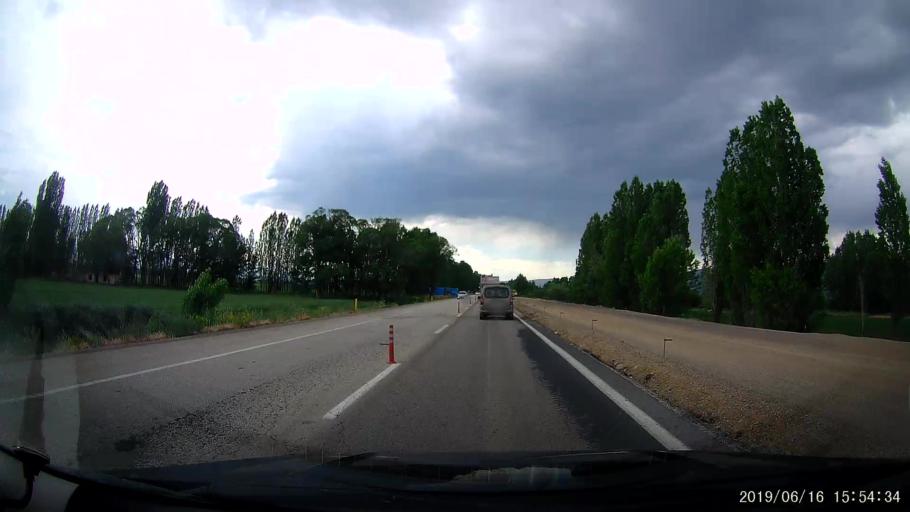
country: TR
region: Erzurum
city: Pasinler
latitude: 39.9776
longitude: 41.6324
